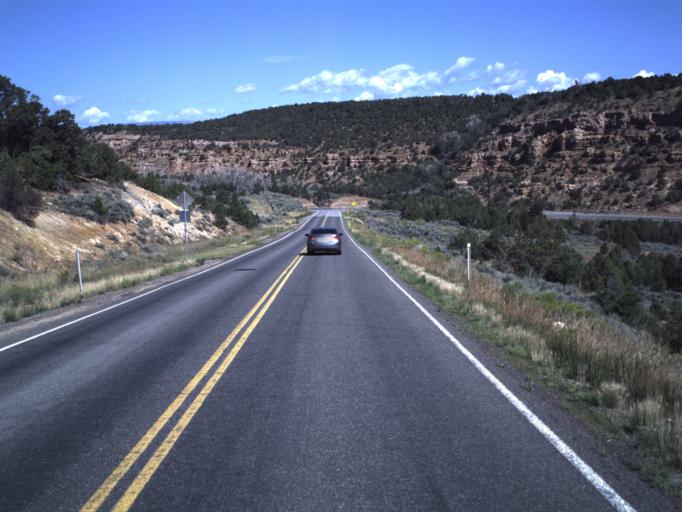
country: US
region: Utah
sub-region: Duchesne County
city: Duchesne
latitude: 40.3554
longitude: -110.3954
